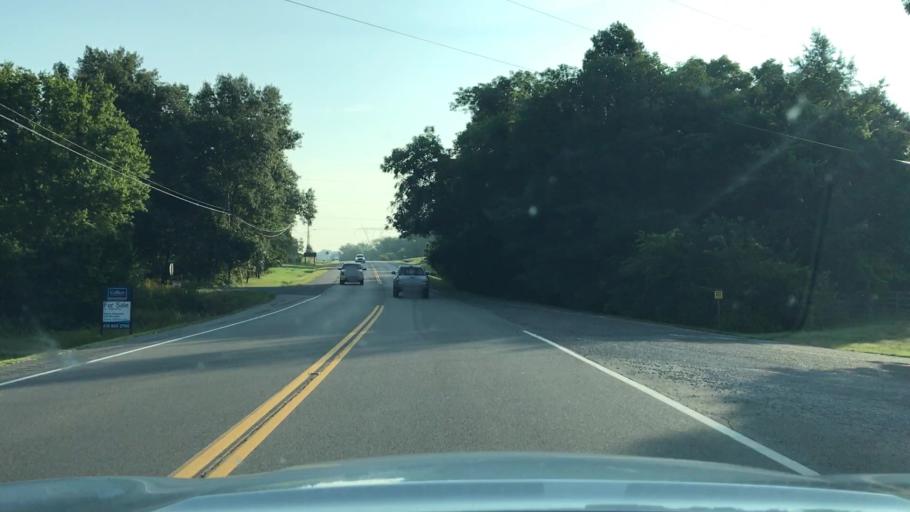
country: US
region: Tennessee
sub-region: Wilson County
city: Rural Hill
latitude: 36.1112
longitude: -86.5278
